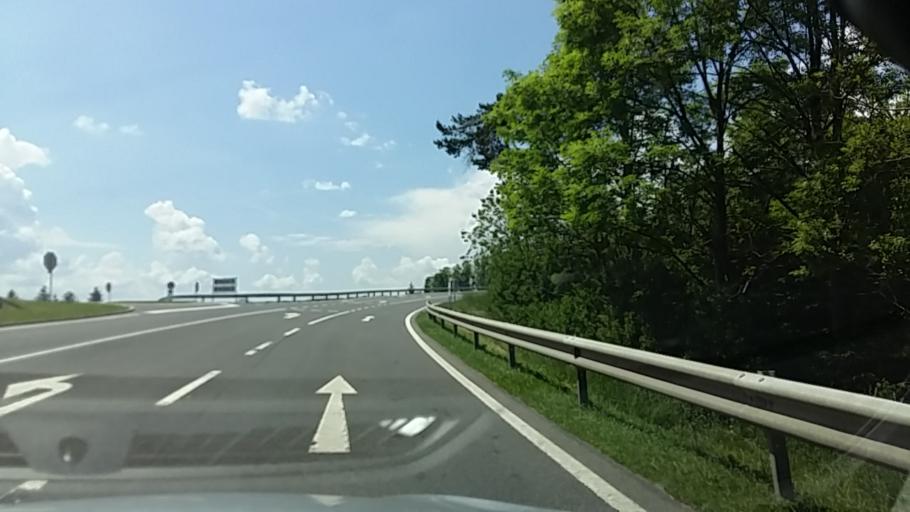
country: AT
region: Burgenland
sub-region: Politischer Bezirk Oberwart
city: Unterkohlstatten
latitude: 47.4001
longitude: 16.2953
